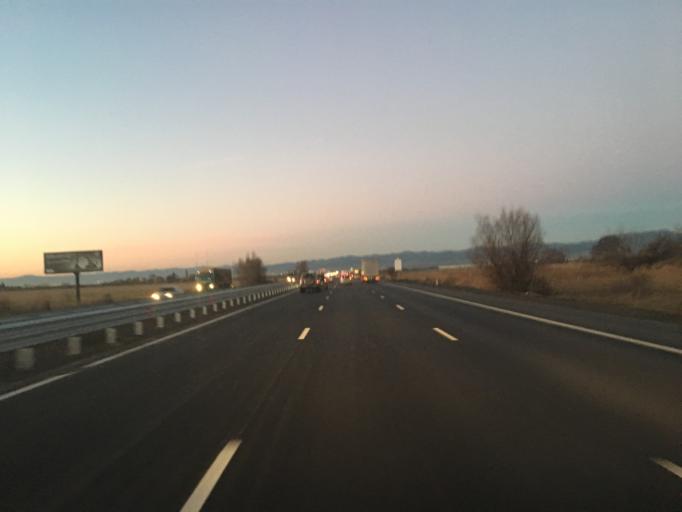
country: BG
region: Sofia-Capital
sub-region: Stolichna Obshtina
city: Sofia
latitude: 42.6889
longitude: 23.4531
